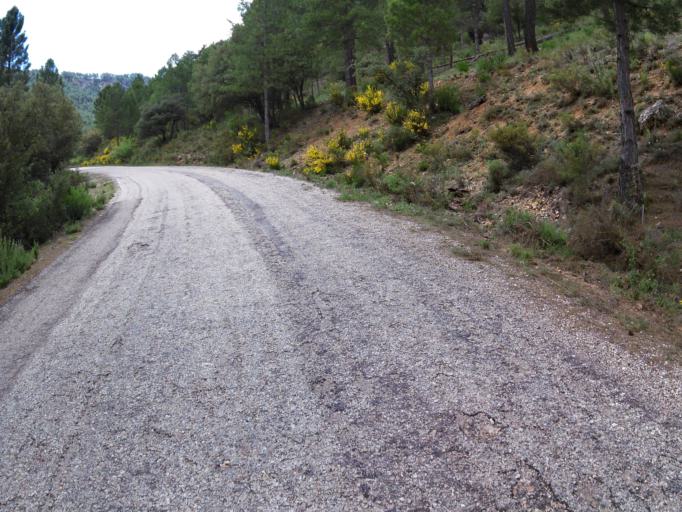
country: ES
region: Castille-La Mancha
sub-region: Provincia de Albacete
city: Paterna del Madera
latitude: 38.5774
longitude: -2.3523
